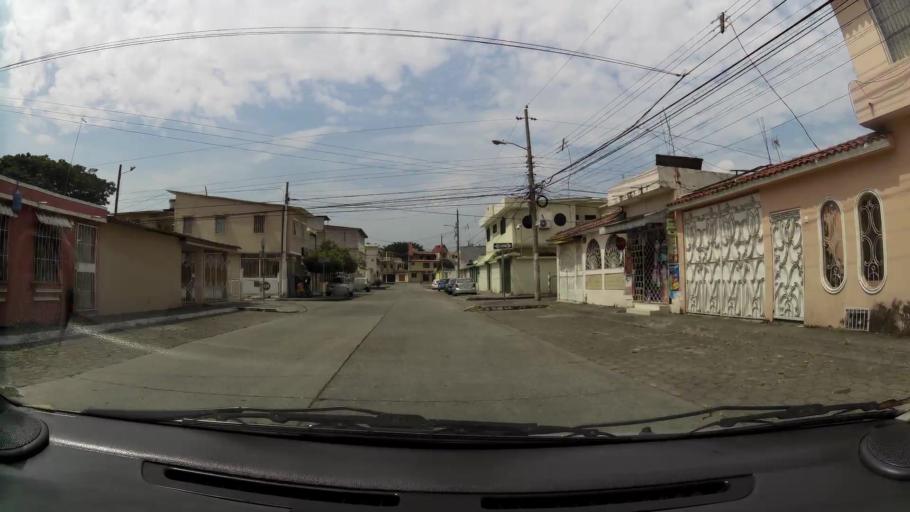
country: EC
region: Guayas
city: Eloy Alfaro
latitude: -2.1353
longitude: -79.9067
